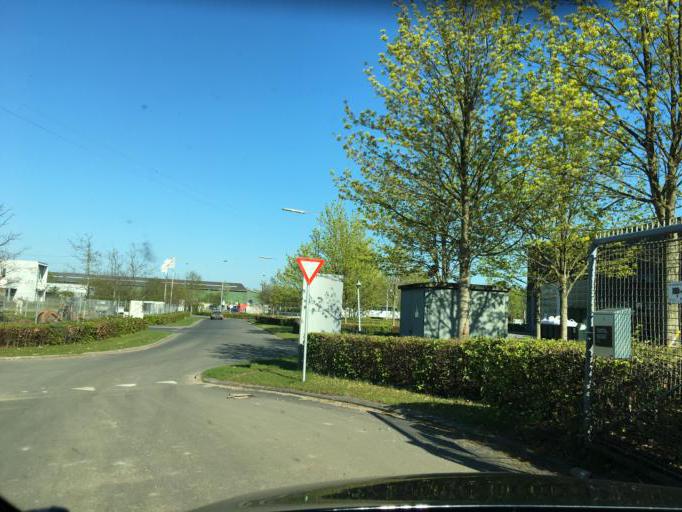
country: DK
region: South Denmark
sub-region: Kolding Kommune
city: Kolding
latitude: 55.5110
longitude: 9.4445
